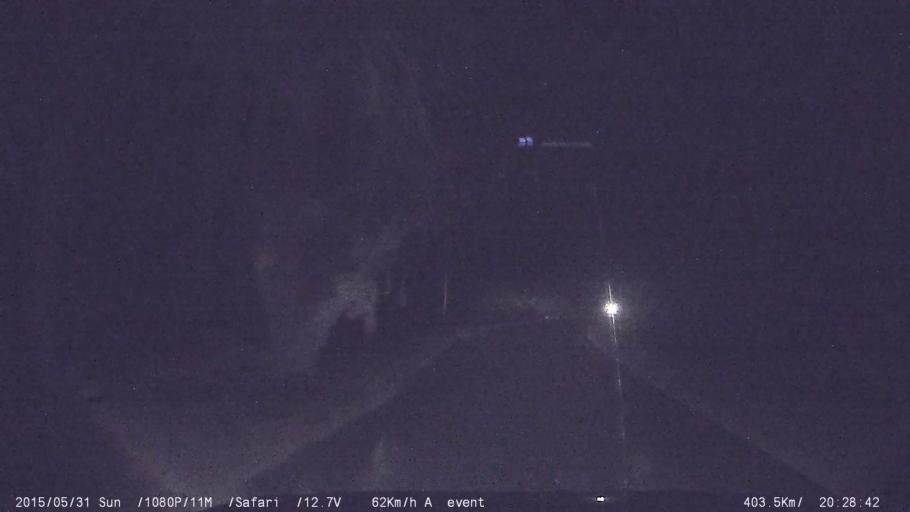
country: IN
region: Karnataka
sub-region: Mandya
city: Malavalli
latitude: 12.4508
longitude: 77.2311
